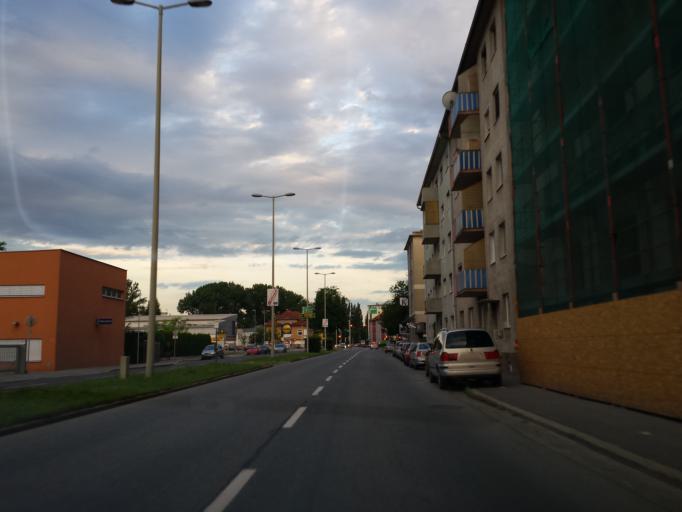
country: AT
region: Styria
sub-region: Graz Stadt
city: Goesting
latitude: 47.0899
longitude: 15.4093
